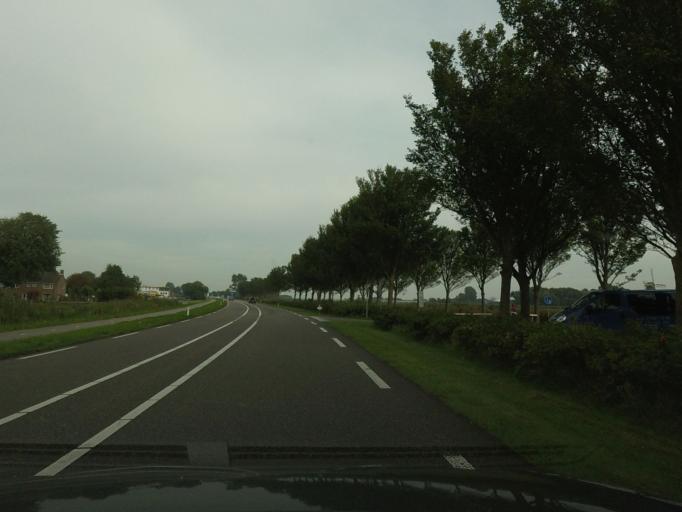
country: NL
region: North Holland
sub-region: Gemeente Schagen
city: Schagen
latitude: 52.8560
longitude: 4.8292
